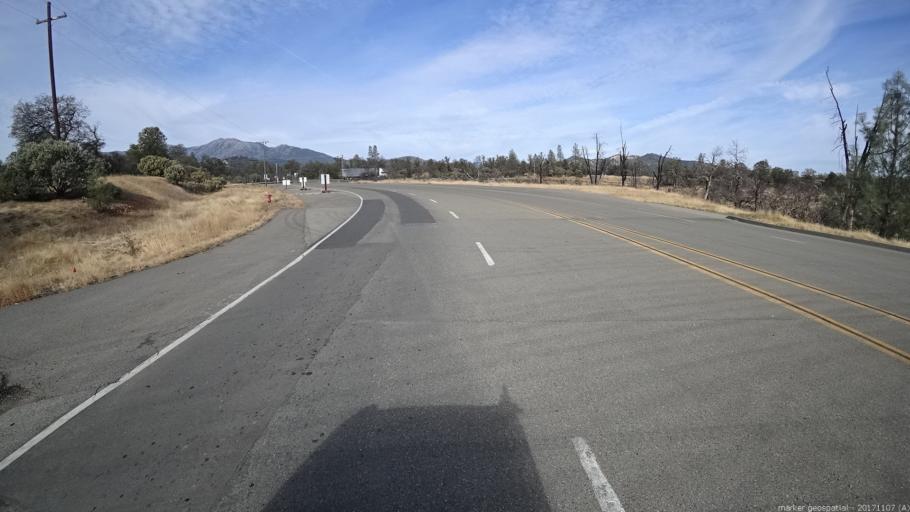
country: US
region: California
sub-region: Shasta County
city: Shasta
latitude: 40.4891
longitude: -122.5386
